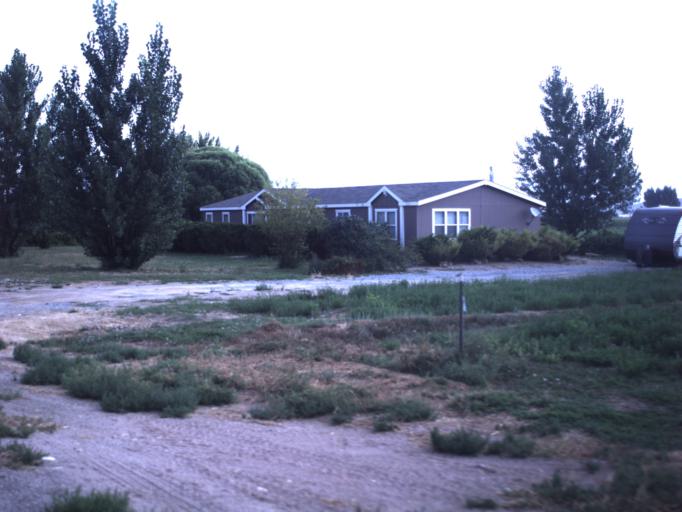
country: US
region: Utah
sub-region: Uintah County
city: Naples
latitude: 40.3823
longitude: -109.3458
